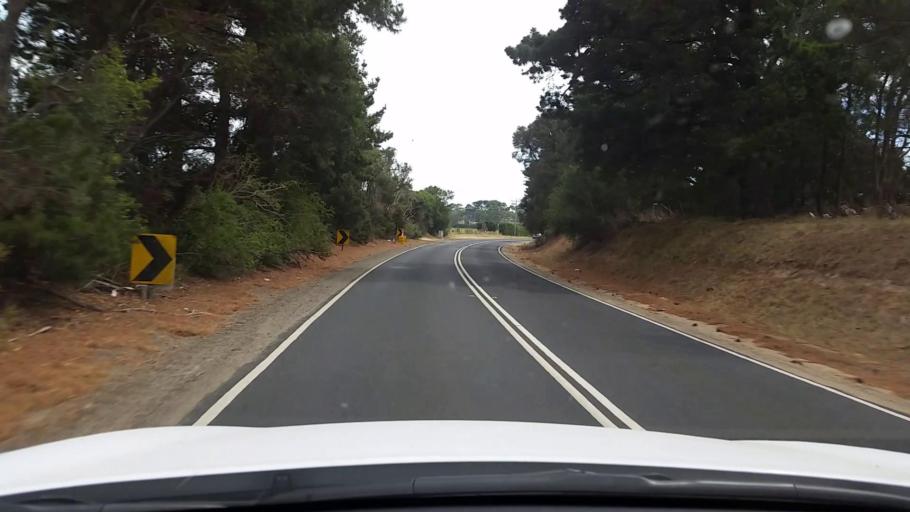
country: AU
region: Victoria
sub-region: Mornington Peninsula
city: Tootgarook
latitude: -38.4256
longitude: 144.8873
